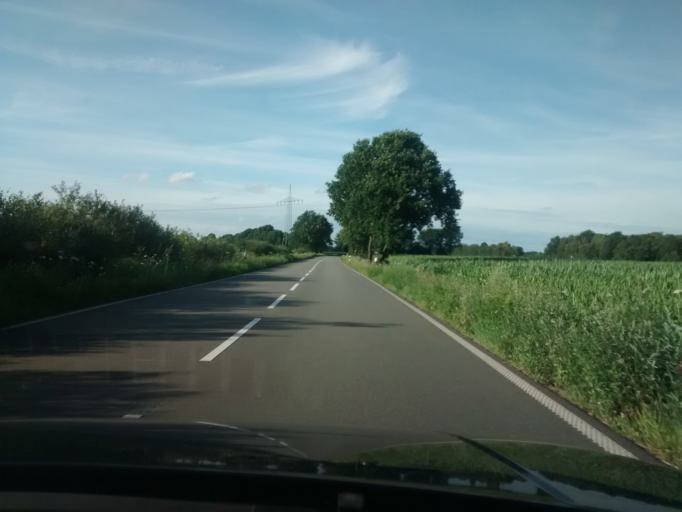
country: DE
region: Lower Saxony
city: Hoogstede
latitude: 52.6302
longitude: 6.9837
